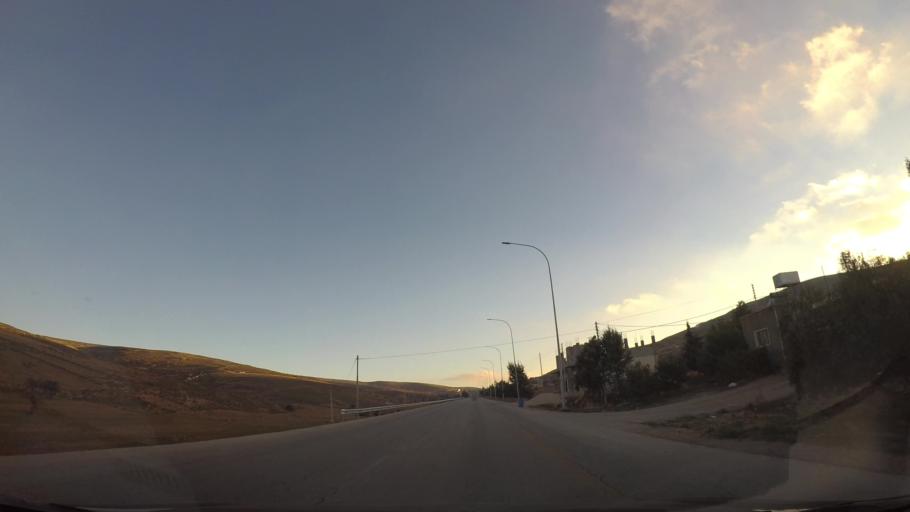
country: JO
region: Ma'an
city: Petra
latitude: 30.4304
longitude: 35.5154
